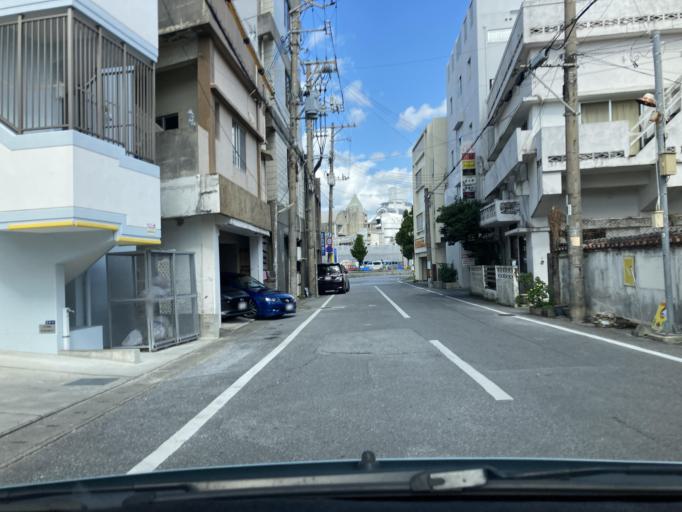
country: JP
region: Okinawa
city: Okinawa
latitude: 26.3287
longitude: 127.7946
